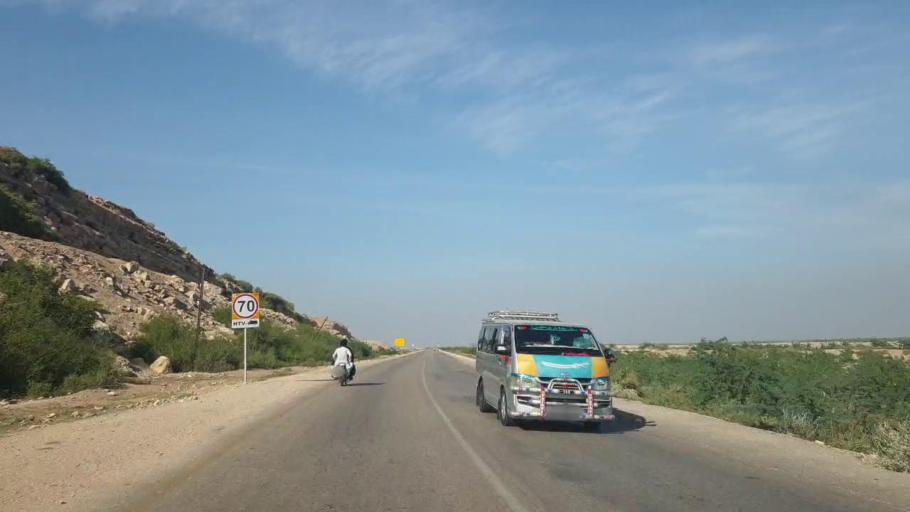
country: PK
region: Sindh
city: Sehwan
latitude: 26.3662
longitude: 67.8737
